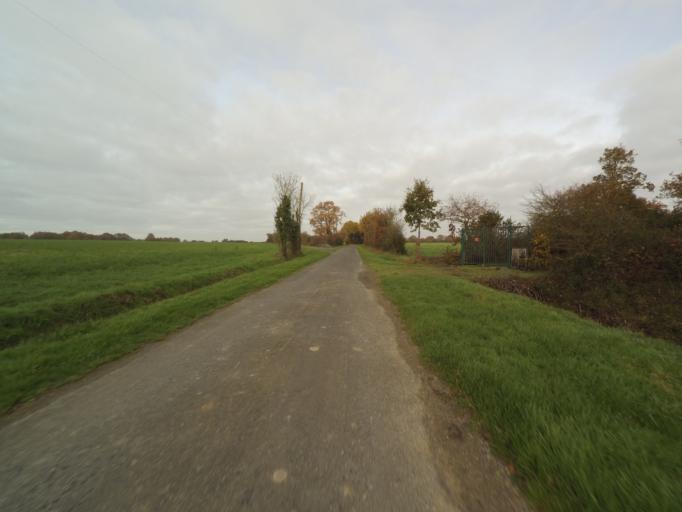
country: FR
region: Pays de la Loire
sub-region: Departement de la Loire-Atlantique
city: La Planche
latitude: 47.0067
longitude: -1.3906
